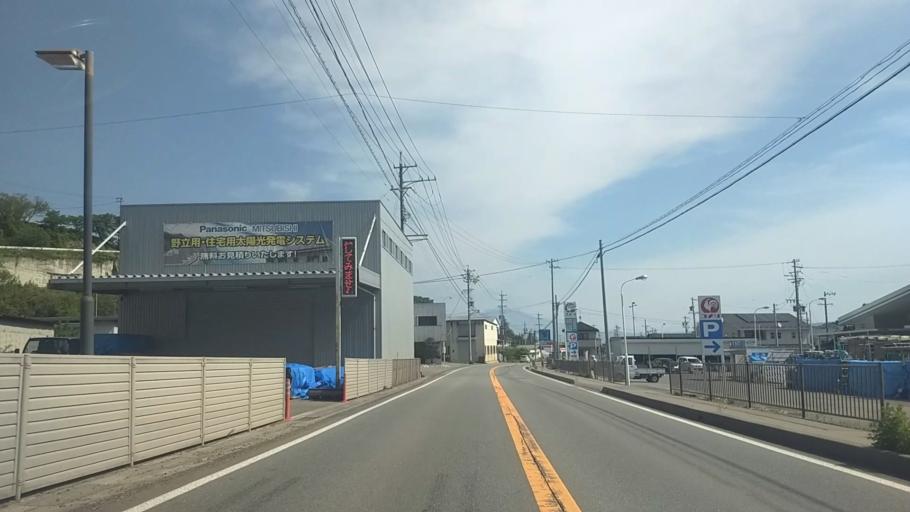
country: JP
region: Nagano
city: Saku
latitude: 36.1256
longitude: 138.4690
